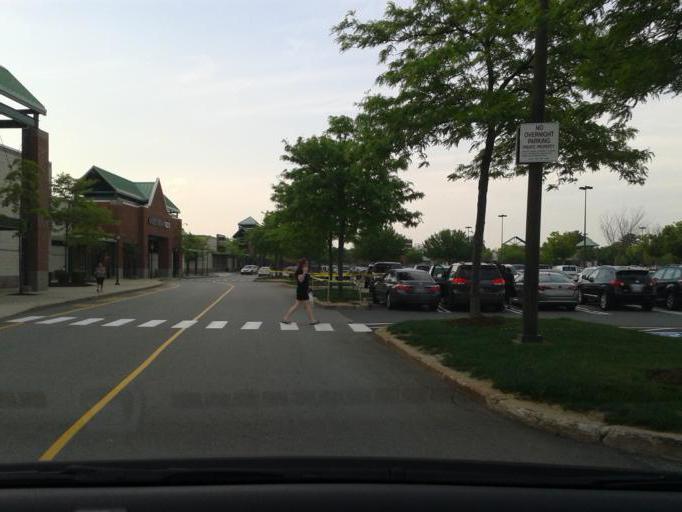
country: US
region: Massachusetts
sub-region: Middlesex County
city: Framingham
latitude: 42.3013
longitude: -71.3958
